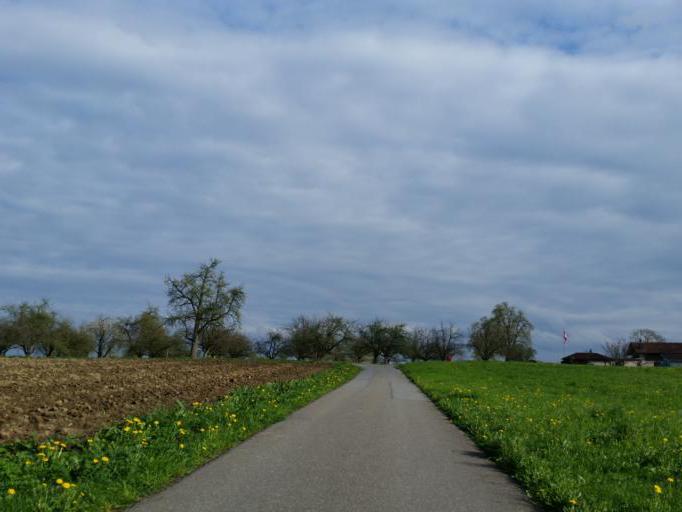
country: CH
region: Thurgau
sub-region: Arbon District
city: Uttwil
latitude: 47.5804
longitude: 9.3411
